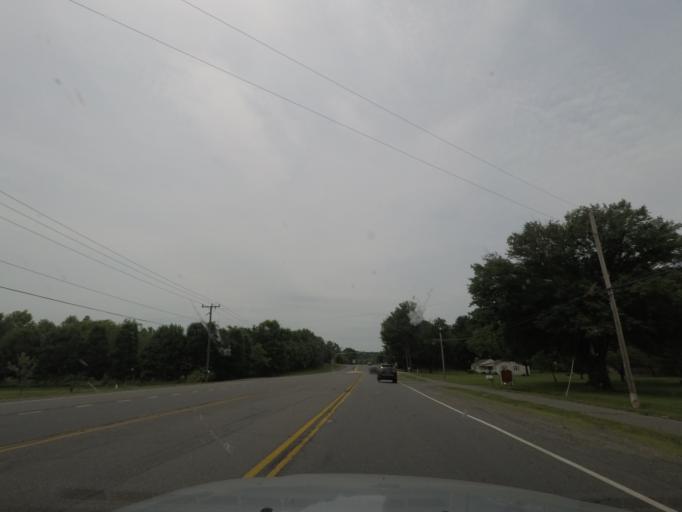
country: US
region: Virginia
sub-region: Loudoun County
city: Leesburg
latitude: 39.0848
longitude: -77.5939
